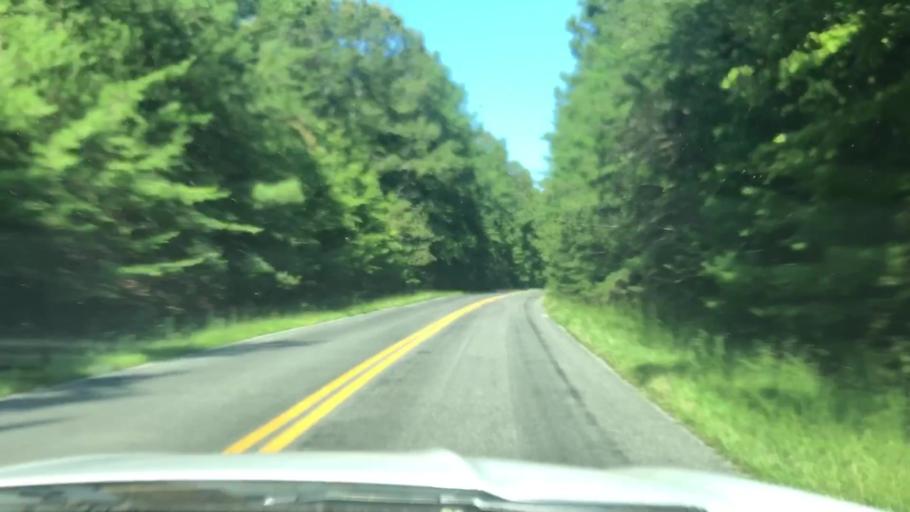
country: US
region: Virginia
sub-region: New Kent County
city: New Kent
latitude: 37.4836
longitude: -76.9265
